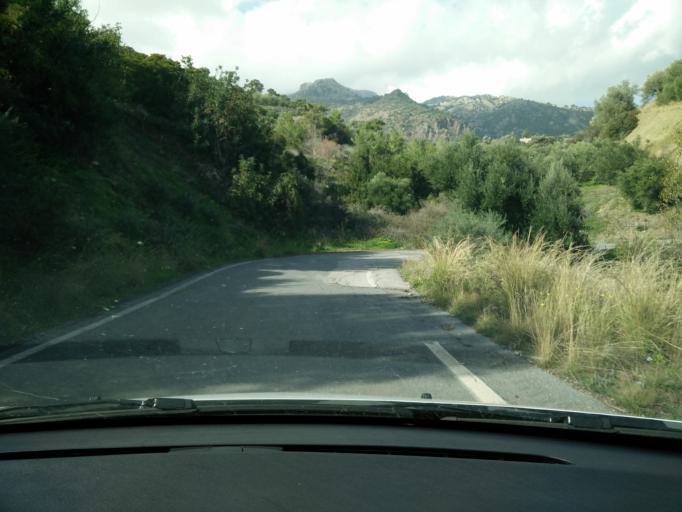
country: GR
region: Crete
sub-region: Nomos Lasithiou
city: Gra Liyia
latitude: 35.0300
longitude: 25.5794
